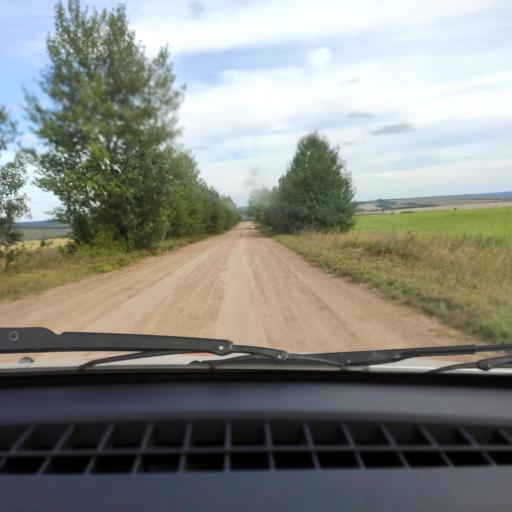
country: RU
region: Bashkortostan
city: Blagoveshchensk
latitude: 55.0992
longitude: 55.8077
